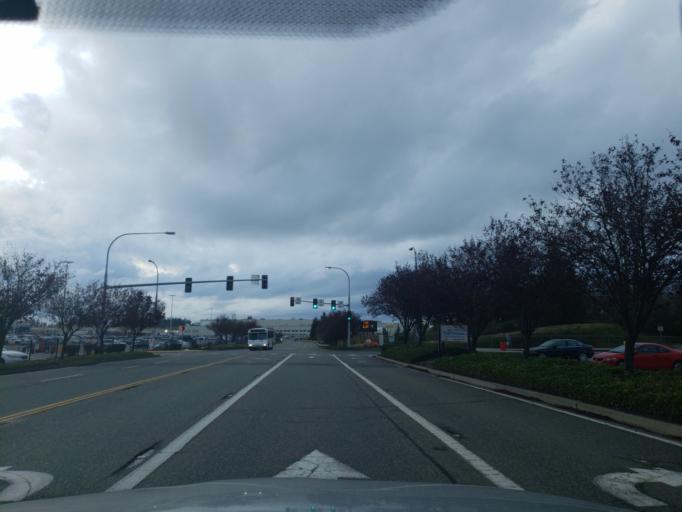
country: US
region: Washington
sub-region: Snohomish County
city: Mukilteo
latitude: 47.9325
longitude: -122.2728
